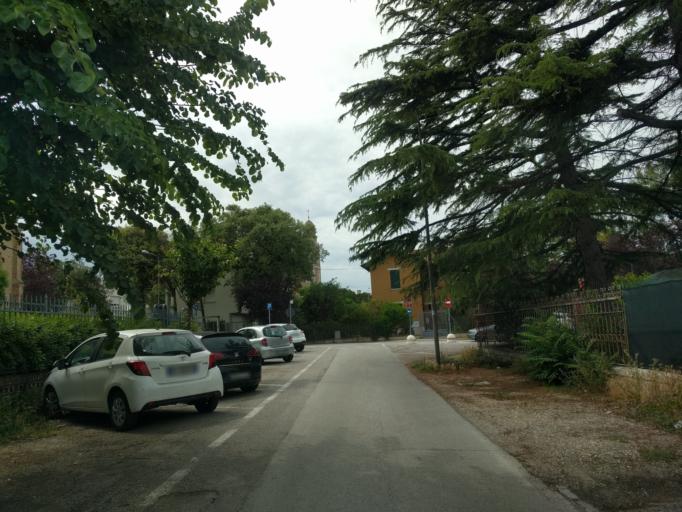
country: IT
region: The Marches
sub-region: Provincia di Pesaro e Urbino
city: Fano
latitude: 43.8402
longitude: 13.0231
